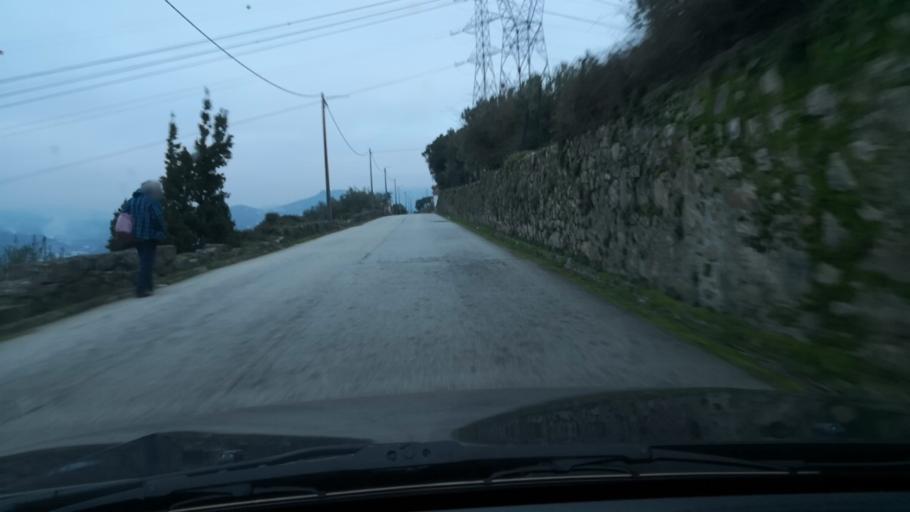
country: PT
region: Vila Real
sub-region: Peso da Regua
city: Peso da Regua
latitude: 41.1333
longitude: -7.7962
